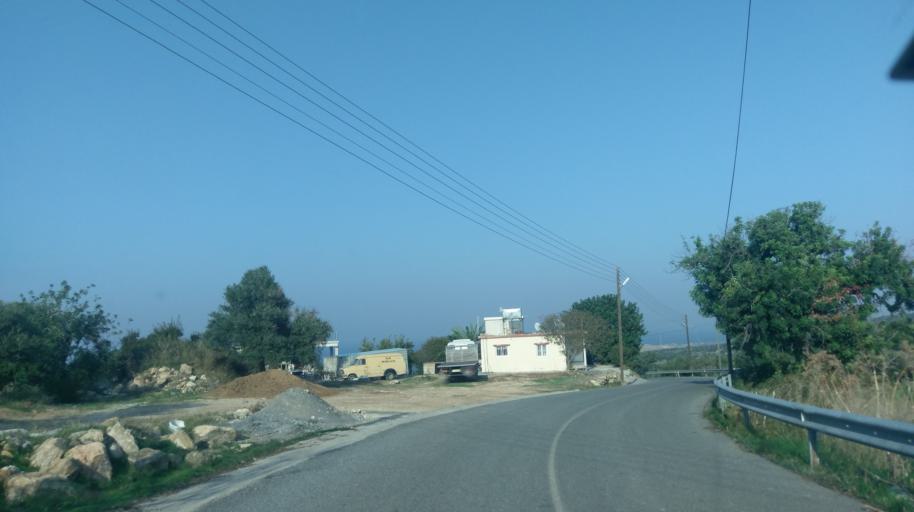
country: CY
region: Ammochostos
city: Leonarisso
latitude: 35.5467
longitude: 34.2267
